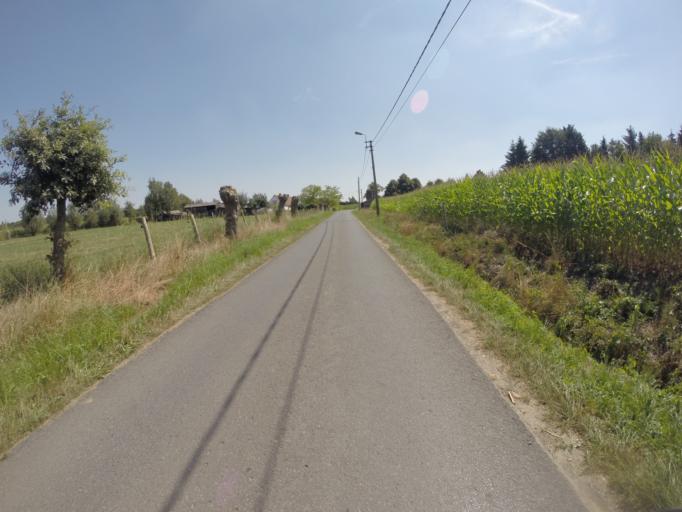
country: BE
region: Flanders
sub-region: Provincie Oost-Vlaanderen
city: Knesselare
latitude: 51.1439
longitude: 3.4381
